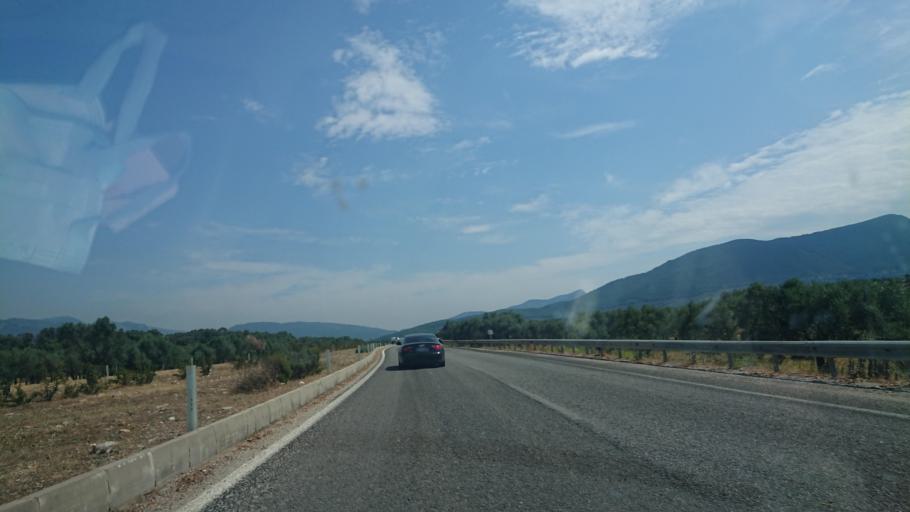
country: TR
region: Izmir
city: Dagkizilca
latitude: 38.2808
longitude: 27.4004
